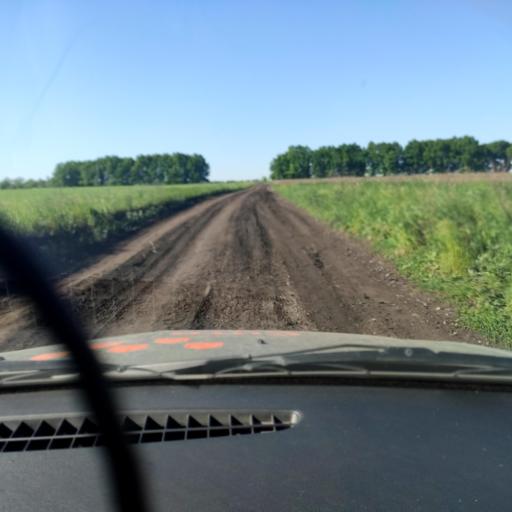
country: RU
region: Bashkortostan
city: Avdon
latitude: 54.5599
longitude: 55.8262
